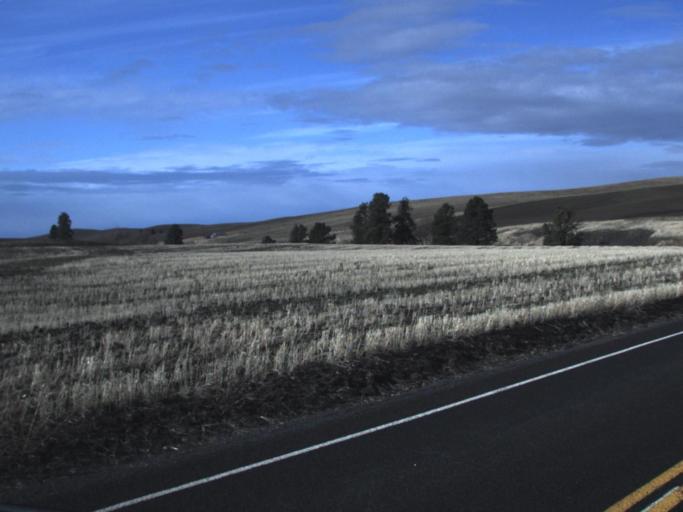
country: US
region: Washington
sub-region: Whitman County
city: Pullman
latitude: 46.9267
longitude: -117.1087
